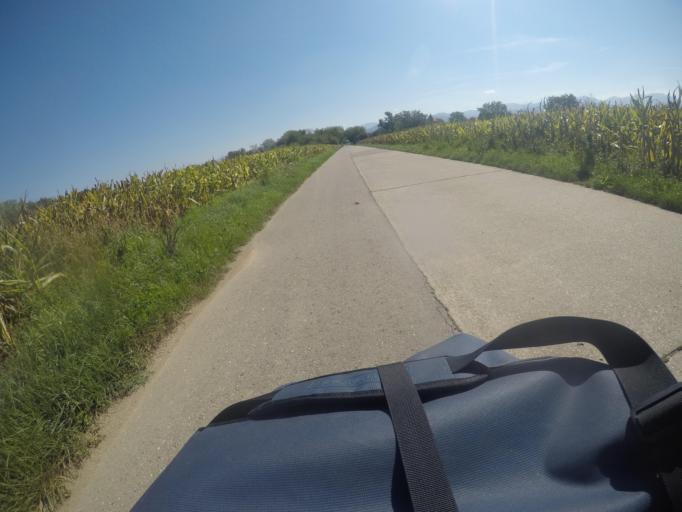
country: DE
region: Baden-Wuerttemberg
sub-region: Freiburg Region
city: Heitersheim
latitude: 47.8771
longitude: 7.6341
